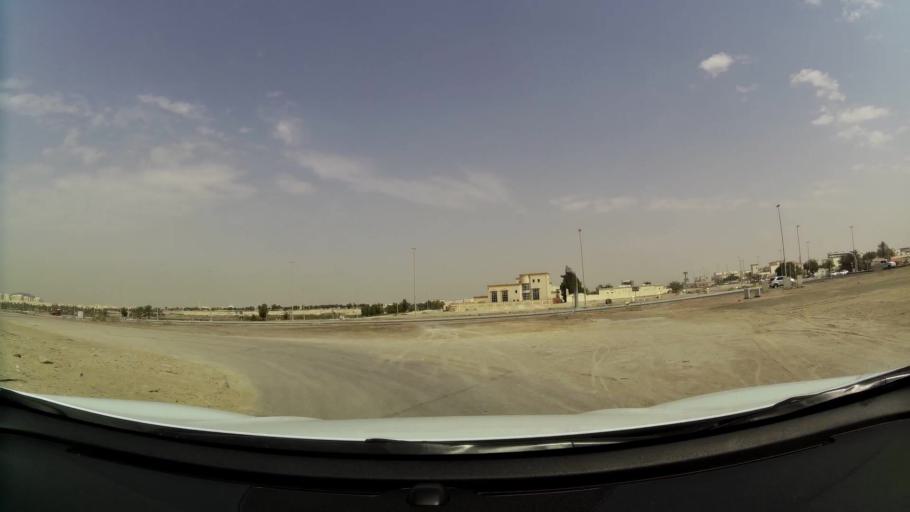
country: AE
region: Abu Dhabi
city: Abu Dhabi
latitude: 24.3008
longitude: 54.6331
